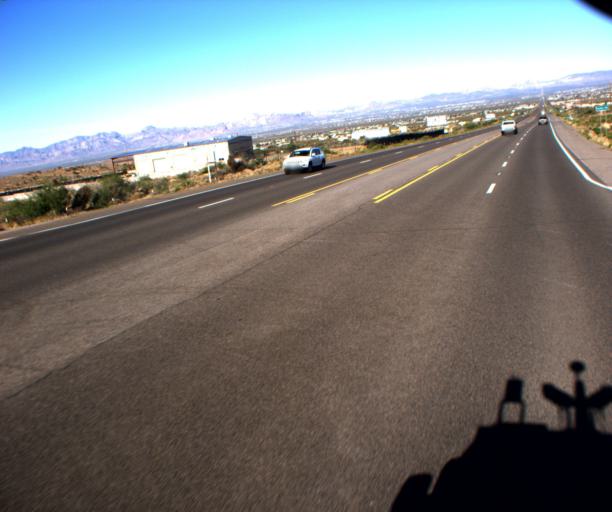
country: US
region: Arizona
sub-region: Mohave County
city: Golden Valley
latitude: 35.2185
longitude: -114.1429
